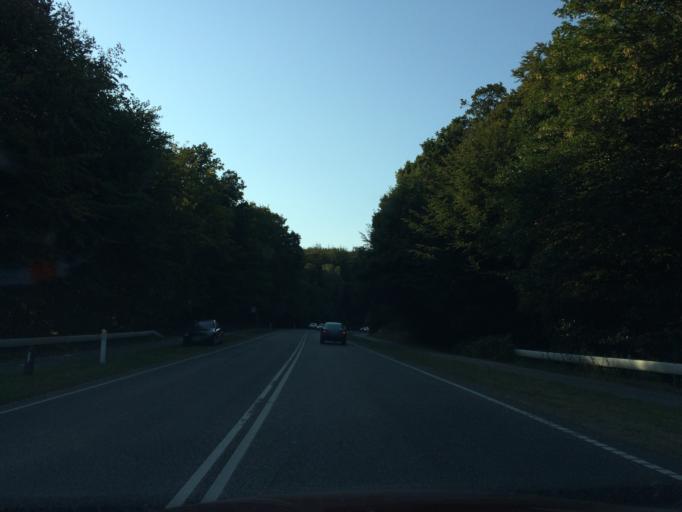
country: DK
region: Central Jutland
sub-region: Silkeborg Kommune
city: Virklund
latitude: 56.1495
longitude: 9.5551
